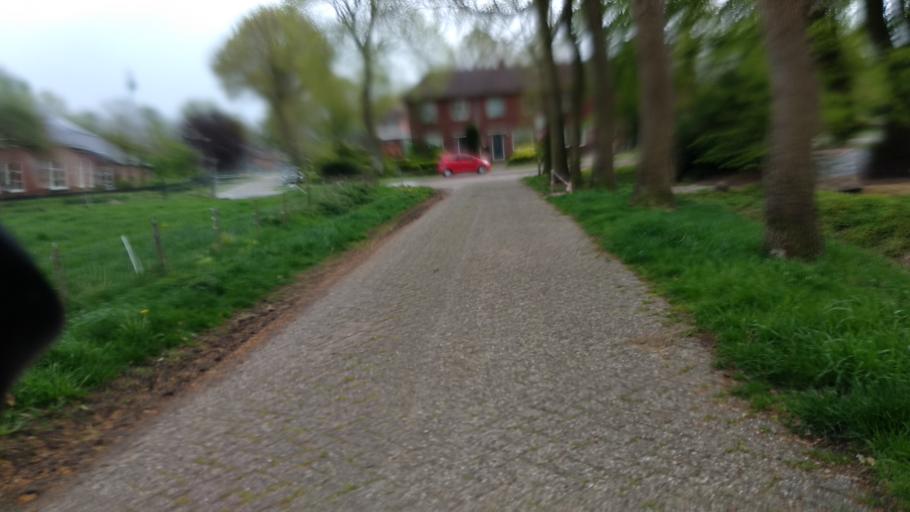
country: NL
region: Drenthe
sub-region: Gemeente Borger-Odoorn
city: Borger
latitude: 52.9314
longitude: 6.8325
